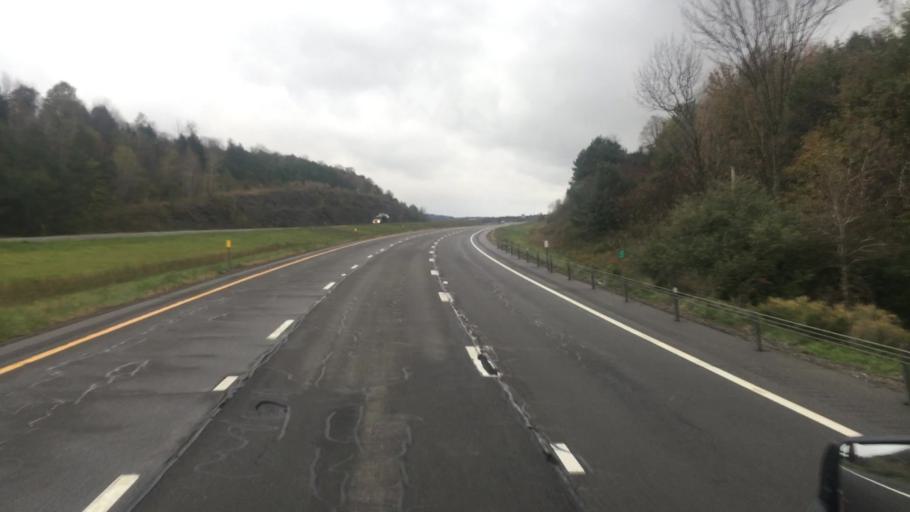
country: US
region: New York
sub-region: Chenango County
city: Greene
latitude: 42.1904
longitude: -75.6536
